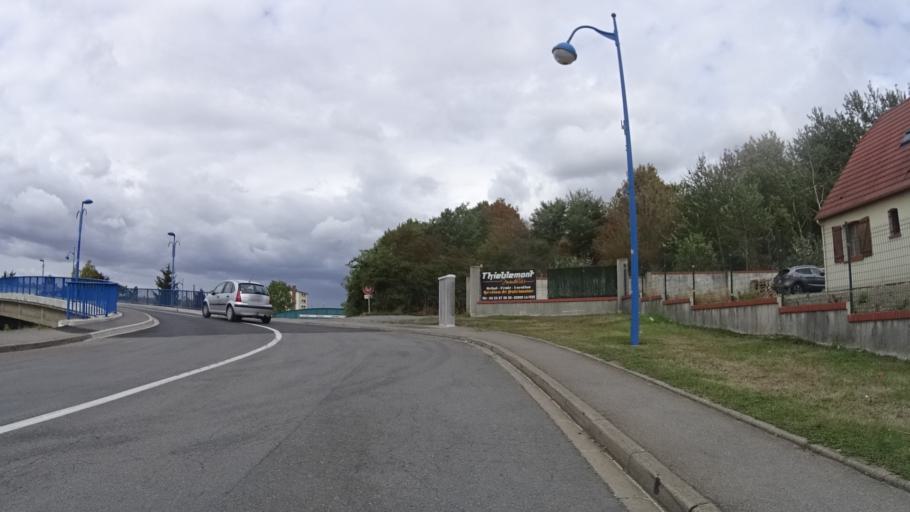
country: FR
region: Picardie
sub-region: Departement de l'Aisne
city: Beautor
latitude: 49.6557
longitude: 3.3470
